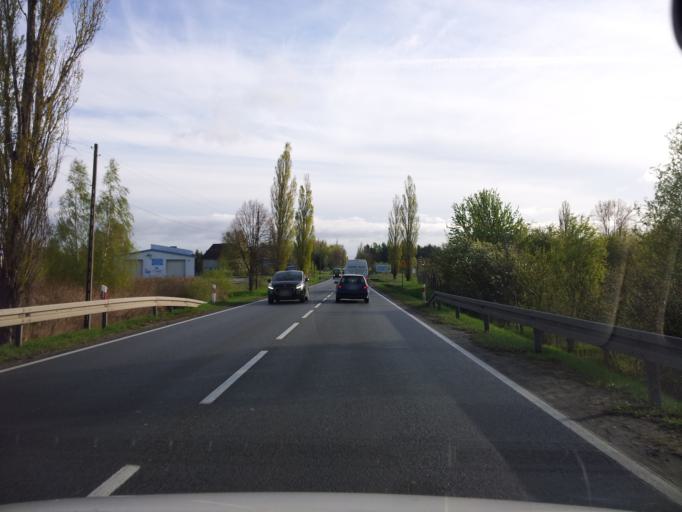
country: PL
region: Lubusz
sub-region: Powiat zielonogorski
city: Nowogrod Bobrzanski
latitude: 51.7995
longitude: 15.2527
